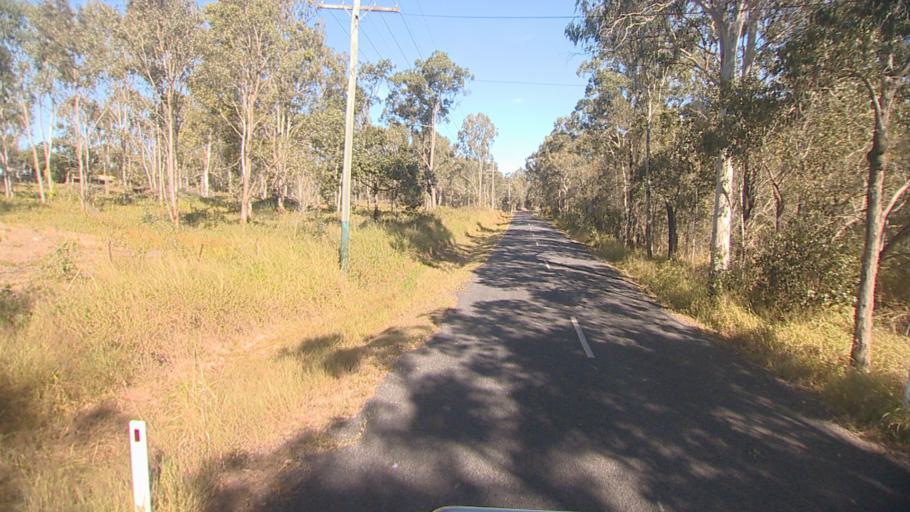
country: AU
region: Queensland
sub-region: Ipswich
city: Springfield Lakes
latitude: -27.7157
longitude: 152.9404
